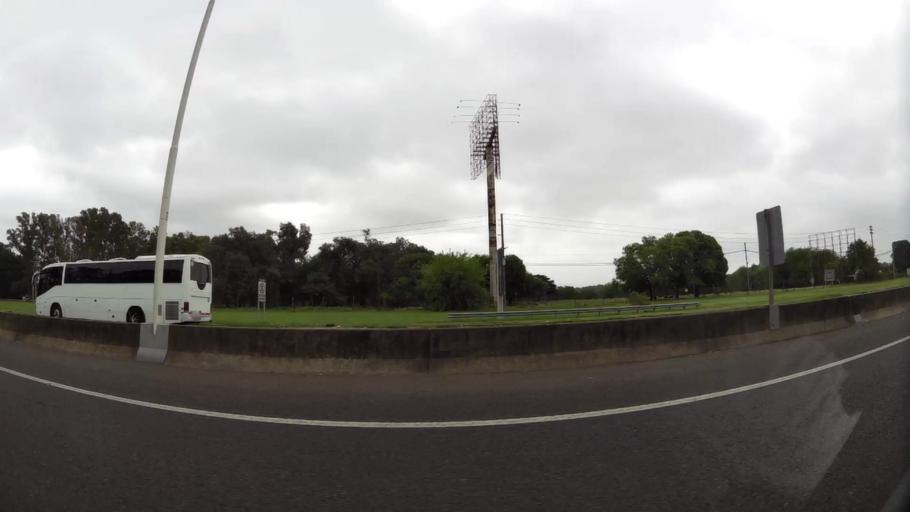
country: AR
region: Buenos Aires
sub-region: Partido de Ezeiza
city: Ezeiza
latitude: -34.7922
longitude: -58.5279
